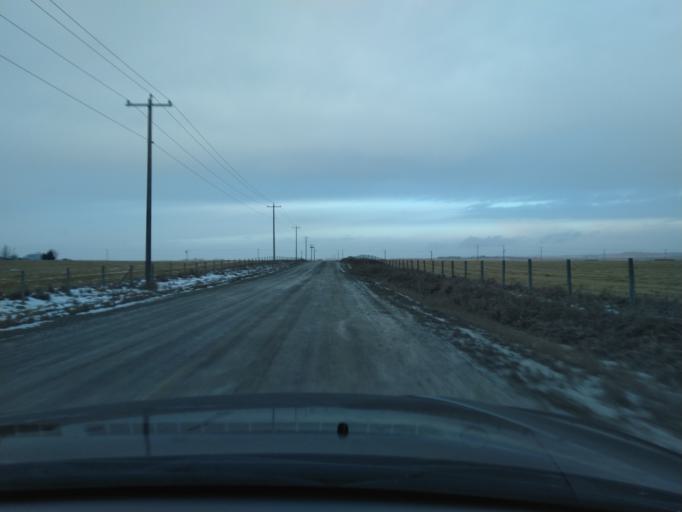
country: CA
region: Alberta
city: Airdrie
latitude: 51.1798
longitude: -114.0248
